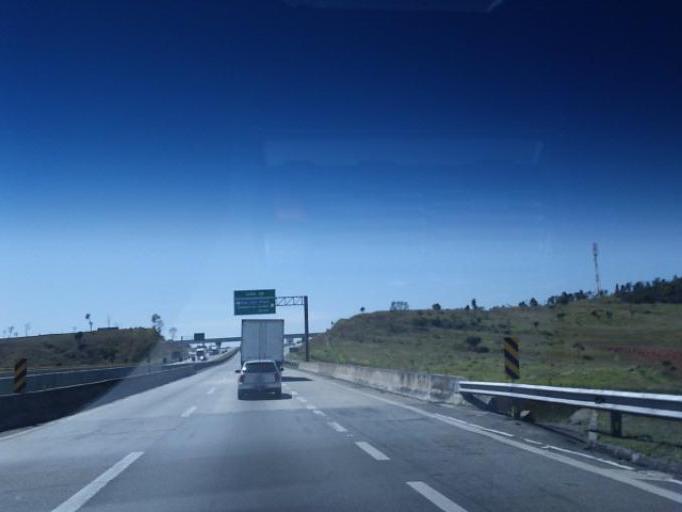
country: BR
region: Sao Paulo
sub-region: Taubate
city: Taubate
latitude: -23.0621
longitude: -45.6256
